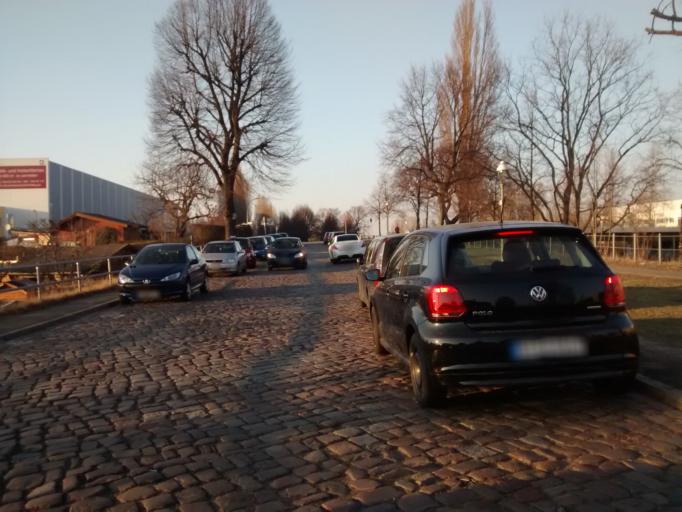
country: DE
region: Berlin
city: Charlottenburg-Nord
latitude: 52.5292
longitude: 13.3135
